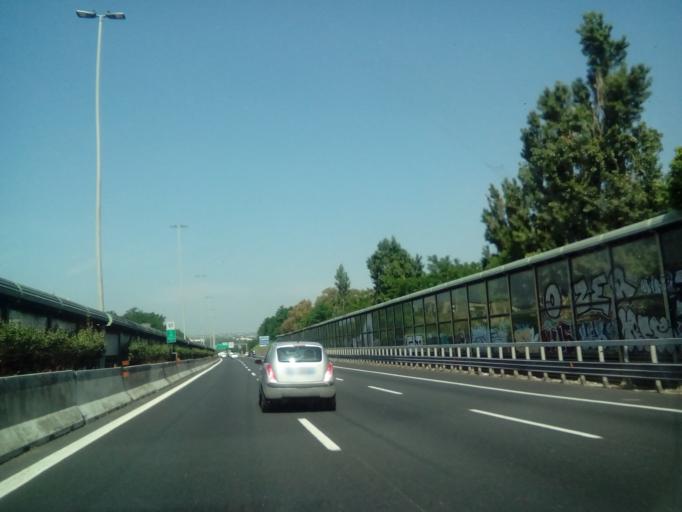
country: IT
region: Latium
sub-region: Citta metropolitana di Roma Capitale
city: Vitinia
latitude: 41.8049
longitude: 12.4290
